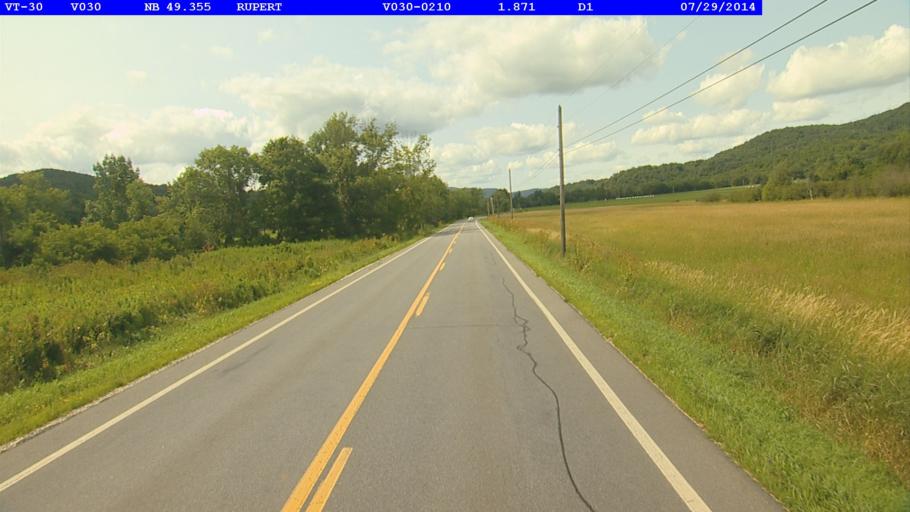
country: US
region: Vermont
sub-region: Bennington County
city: Manchester Center
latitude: 43.2935
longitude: -73.1405
